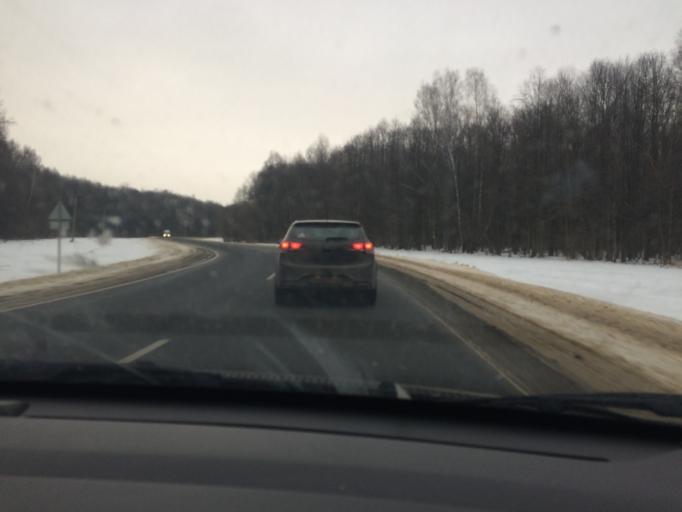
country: RU
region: Tula
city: Venev
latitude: 54.3368
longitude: 38.1159
